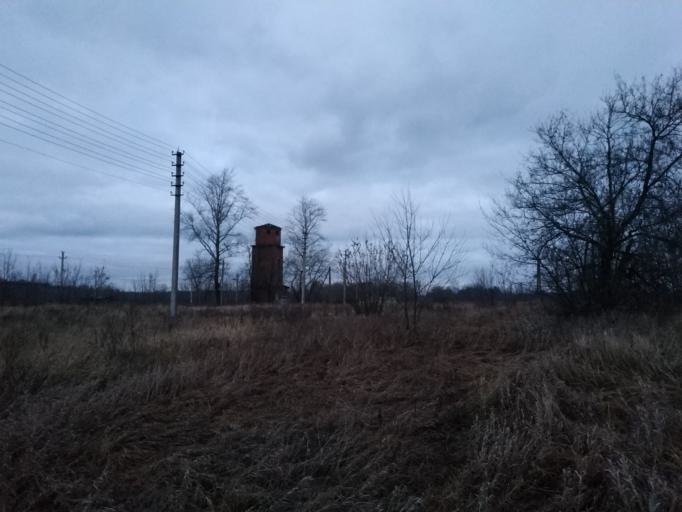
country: RU
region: Moskovskaya
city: Orud'yevo
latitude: 56.4468
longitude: 37.5201
